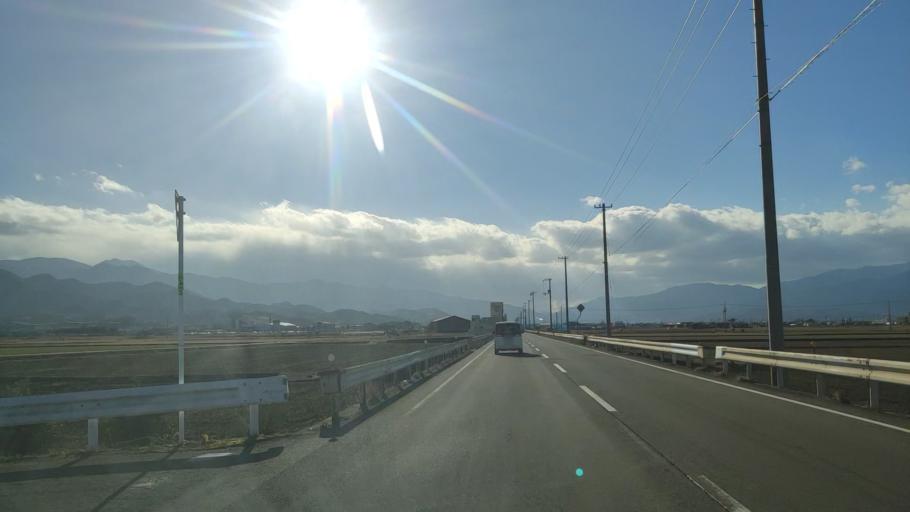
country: JP
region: Ehime
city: Saijo
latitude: 33.9165
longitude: 133.1207
